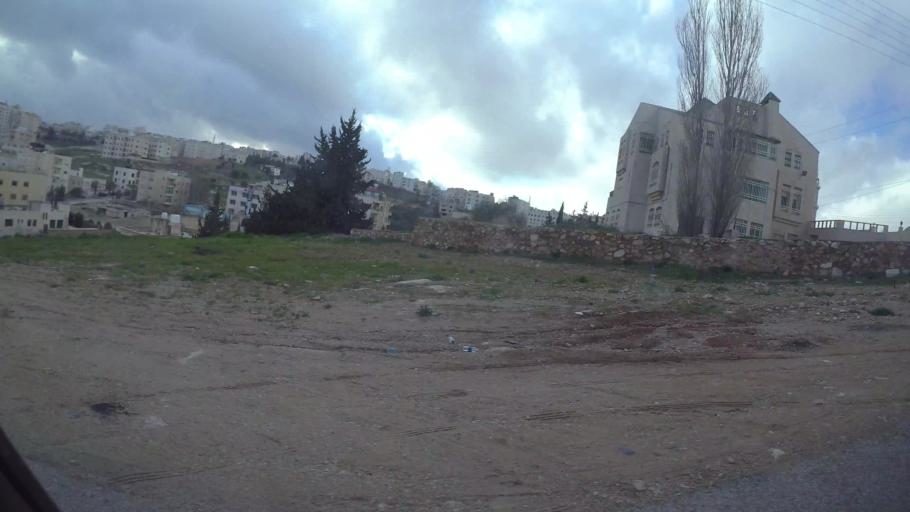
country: JO
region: Amman
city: Al Jubayhah
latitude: 32.0536
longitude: 35.8929
